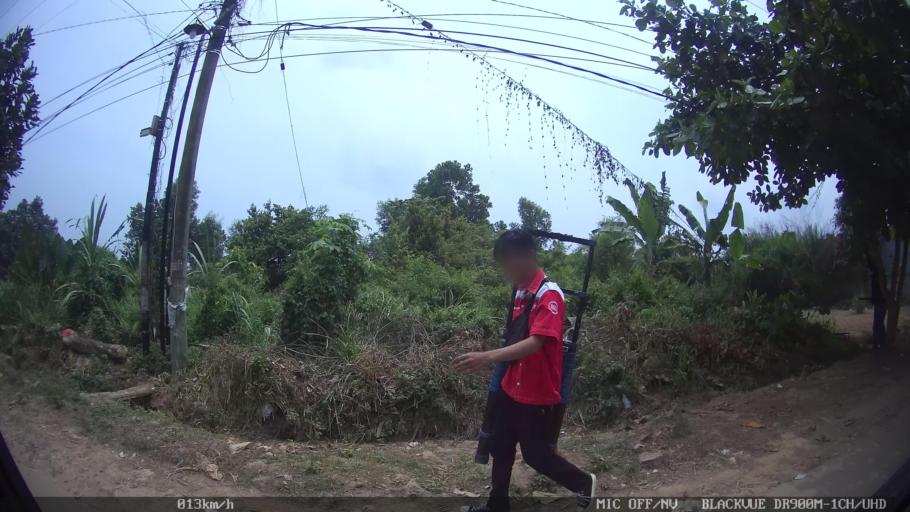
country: ID
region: Lampung
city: Kedaton
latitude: -5.3960
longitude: 105.3219
